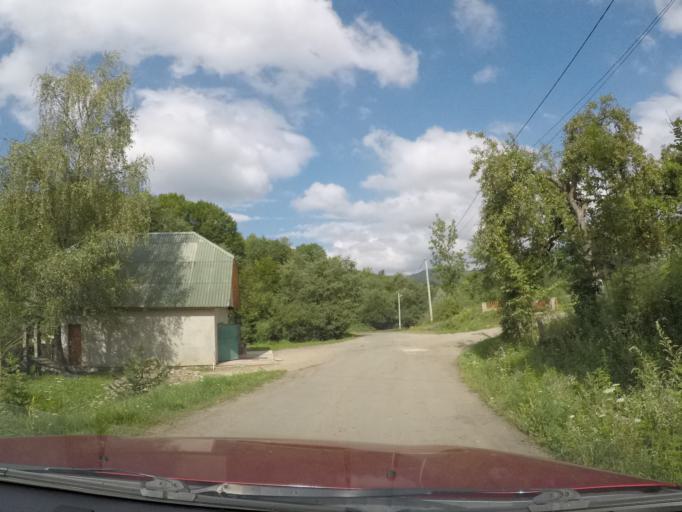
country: UA
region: Zakarpattia
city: Velykyi Bereznyi
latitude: 48.9459
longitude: 22.6796
